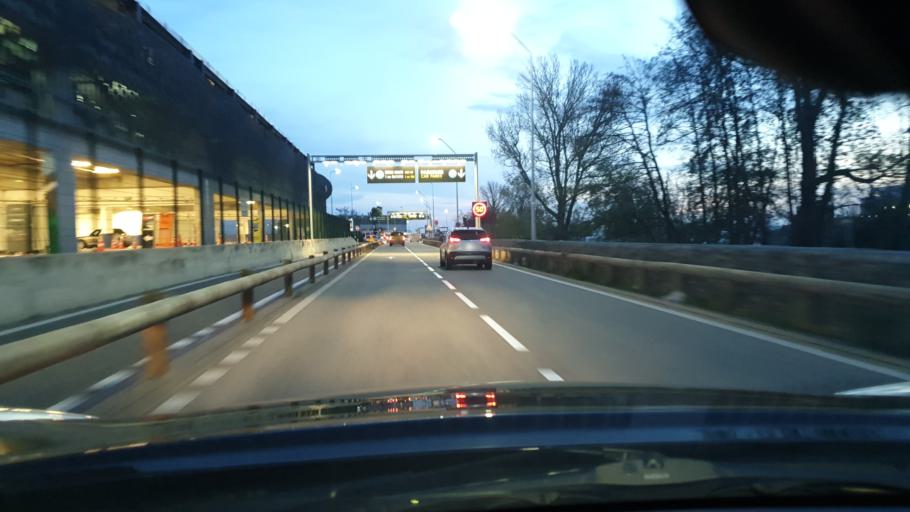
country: FR
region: Provence-Alpes-Cote d'Azur
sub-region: Departement des Alpes-Maritimes
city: Saint-Laurent-du-Var
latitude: 43.6607
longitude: 7.2016
